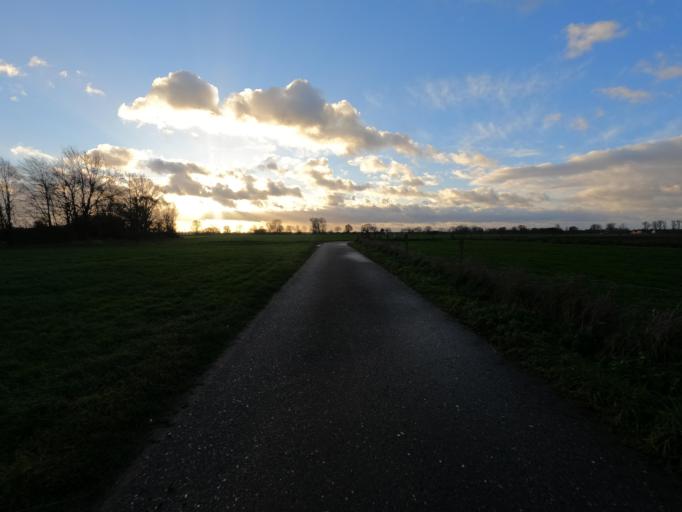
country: DE
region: North Rhine-Westphalia
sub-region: Regierungsbezirk Koln
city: Heinsberg
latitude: 51.0917
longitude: 6.1101
